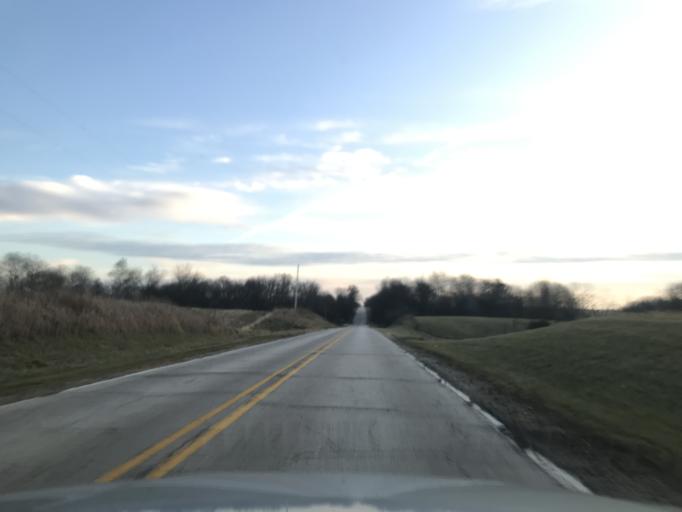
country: US
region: Illinois
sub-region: Henderson County
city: Oquawka
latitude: 40.9629
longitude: -90.8640
